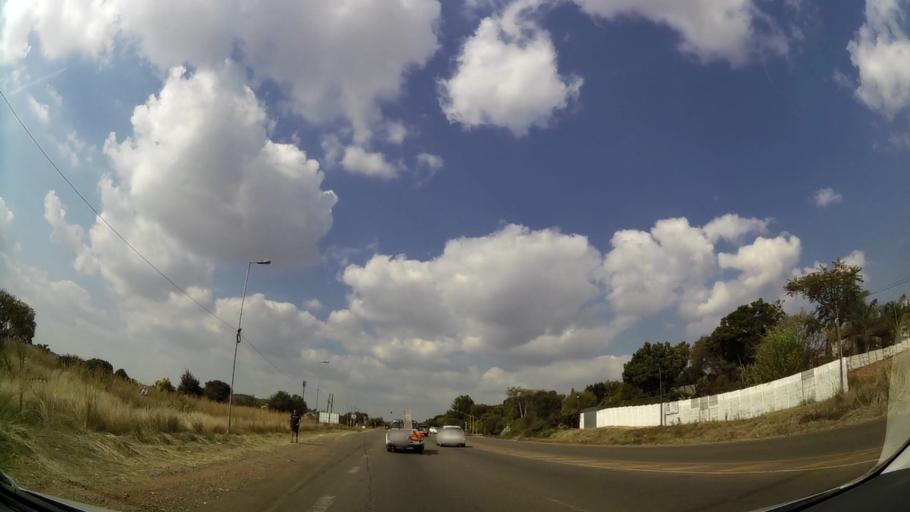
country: ZA
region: Gauteng
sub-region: City of Tshwane Metropolitan Municipality
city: Pretoria
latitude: -25.8018
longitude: 28.3215
